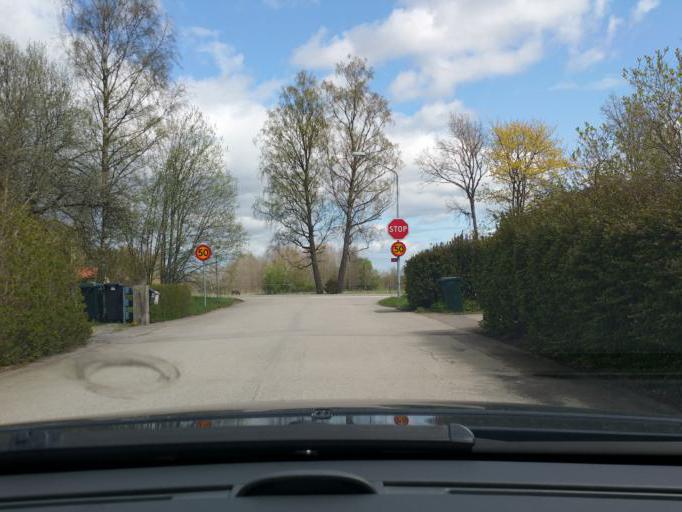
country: SE
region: Kronoberg
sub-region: Vaxjo Kommun
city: Lammhult
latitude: 57.1596
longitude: 14.5905
